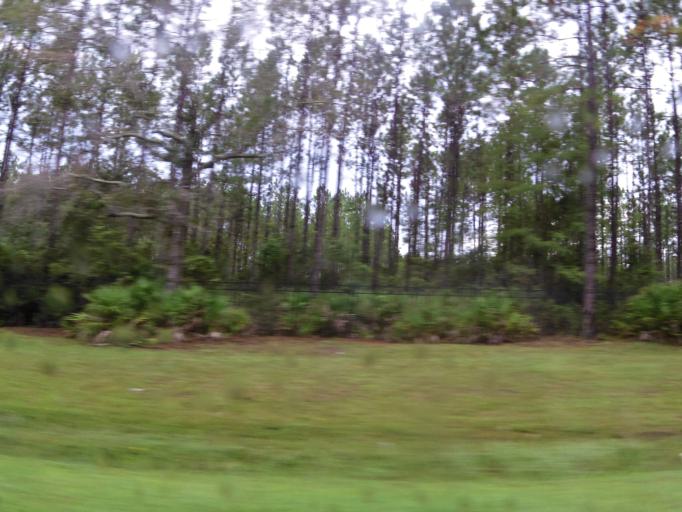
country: US
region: Florida
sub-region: Duval County
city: Baldwin
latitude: 30.4508
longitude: -82.0062
